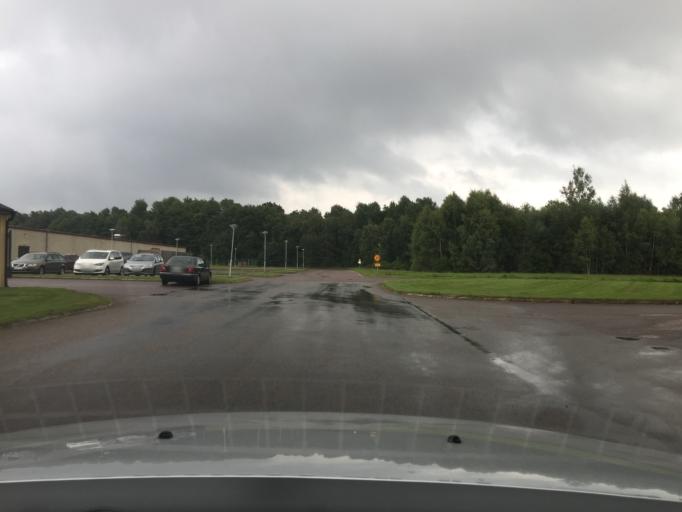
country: SE
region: Skane
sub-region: Hoors Kommun
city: Hoeoer
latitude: 55.9507
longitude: 13.5621
